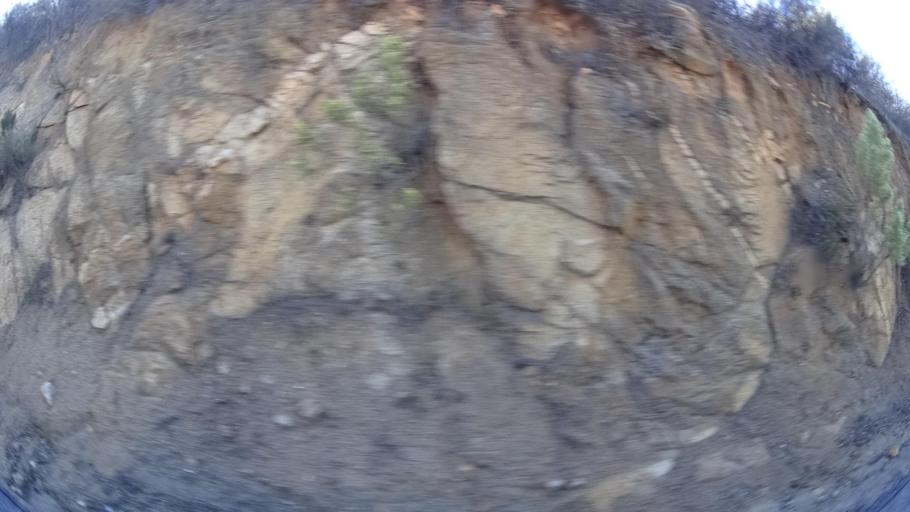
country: US
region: California
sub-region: San Diego County
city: Jamul
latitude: 32.6728
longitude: -116.7739
